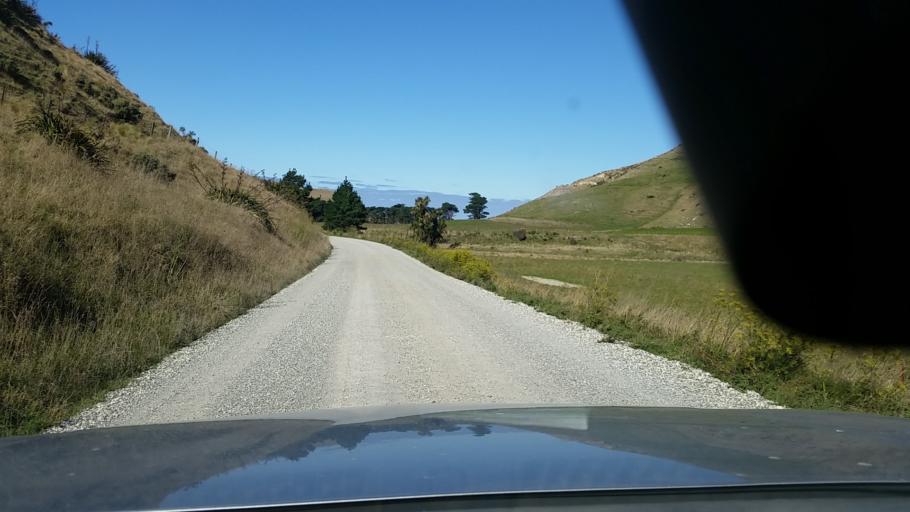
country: NZ
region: Marlborough
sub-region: Marlborough District
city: Blenheim
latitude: -41.8359
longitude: 174.1763
